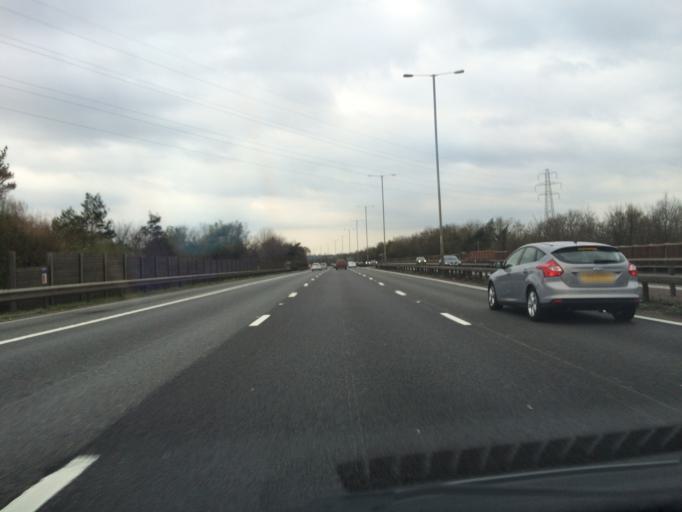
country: GB
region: England
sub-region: Wokingham
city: Winnersh
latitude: 51.4243
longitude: -0.8797
